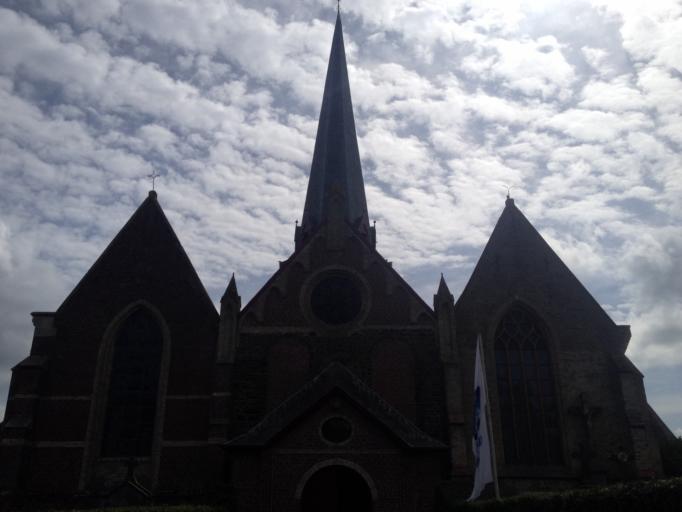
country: FR
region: Nord-Pas-de-Calais
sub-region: Departement du Nord
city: Steenvoorde
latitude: 50.8592
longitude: 2.6195
